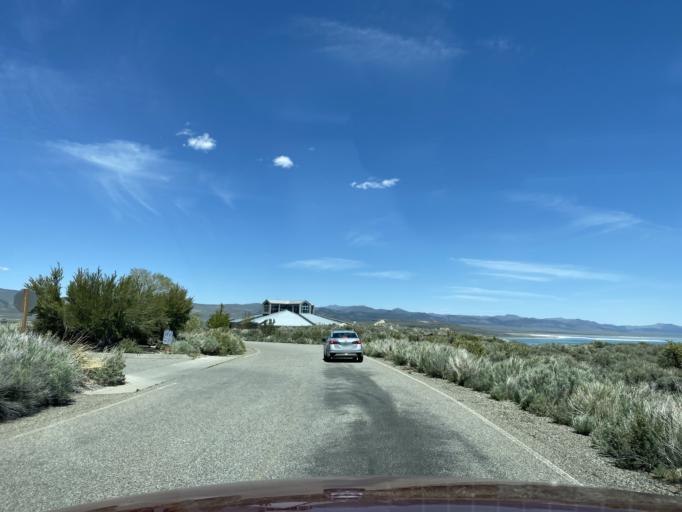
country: US
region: California
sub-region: Mono County
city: Bridgeport
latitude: 37.9655
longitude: -119.1201
